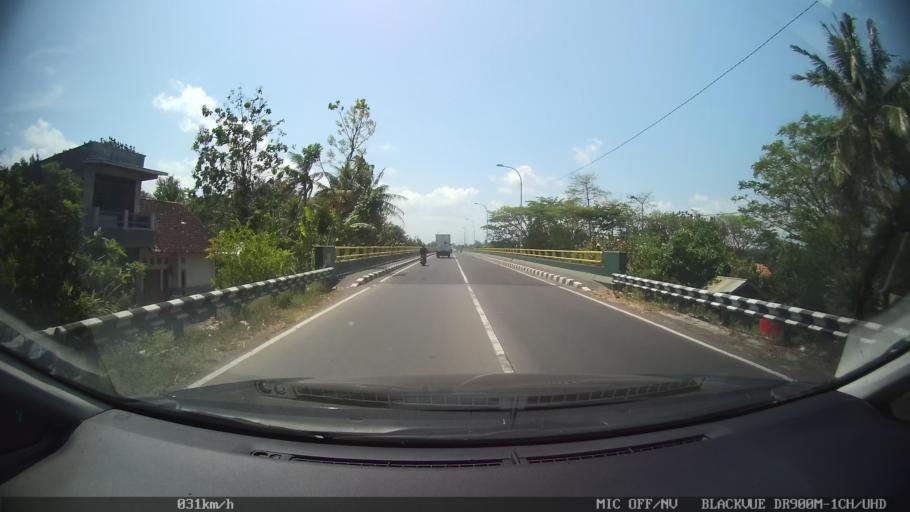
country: ID
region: Daerah Istimewa Yogyakarta
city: Srandakan
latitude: -7.9399
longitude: 110.2397
